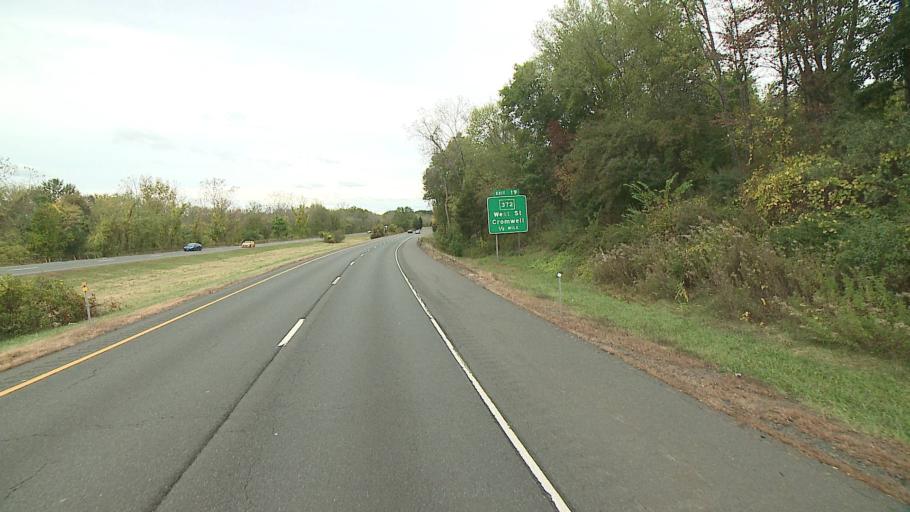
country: US
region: Connecticut
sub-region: Middlesex County
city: Cromwell
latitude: 41.5944
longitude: -72.6673
